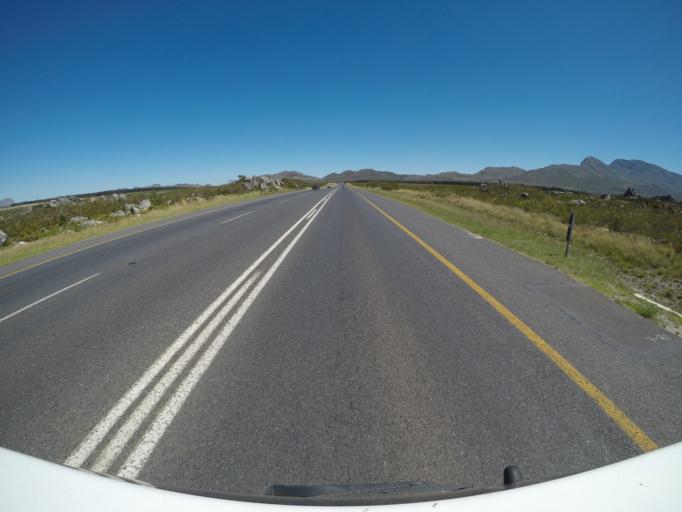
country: ZA
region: Western Cape
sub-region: Overberg District Municipality
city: Grabouw
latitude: -34.1586
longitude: 18.9750
